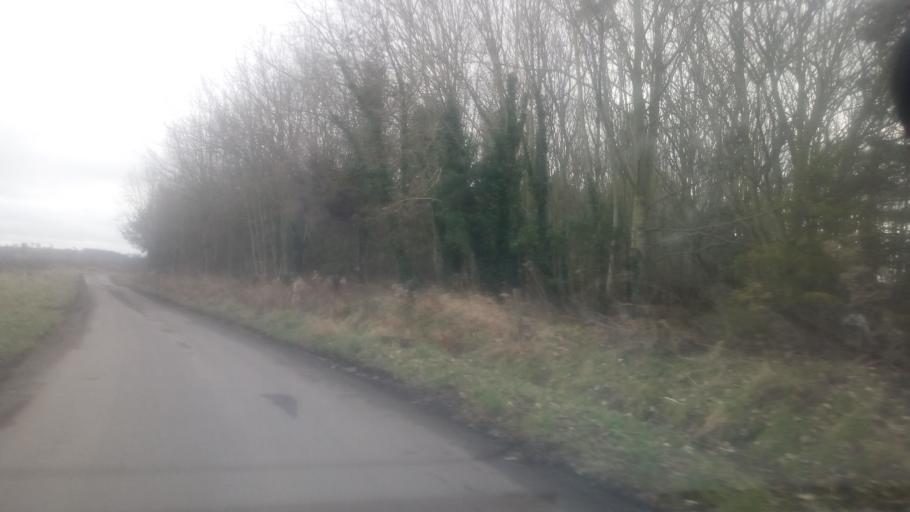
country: GB
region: Scotland
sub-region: The Scottish Borders
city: Kelso
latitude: 55.5657
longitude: -2.4829
